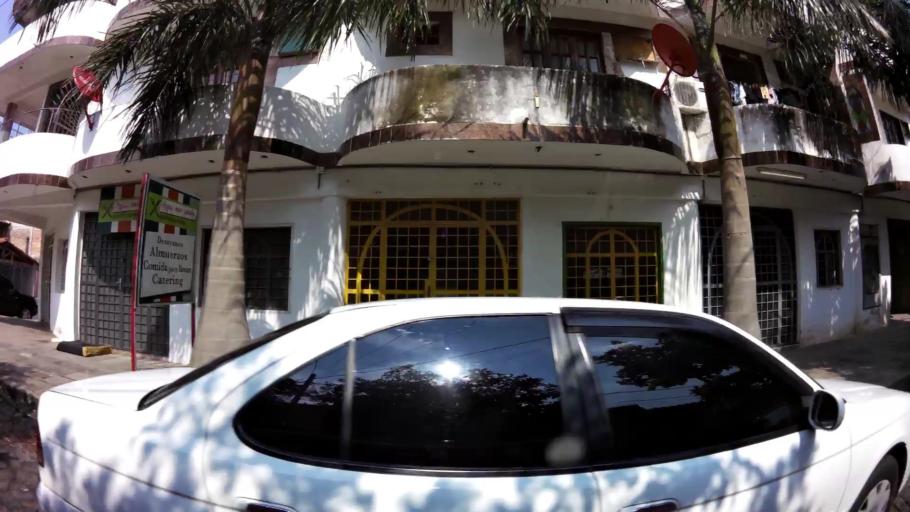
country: PY
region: Presidente Hayes
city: Nanawa
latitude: -25.2855
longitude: -57.6558
